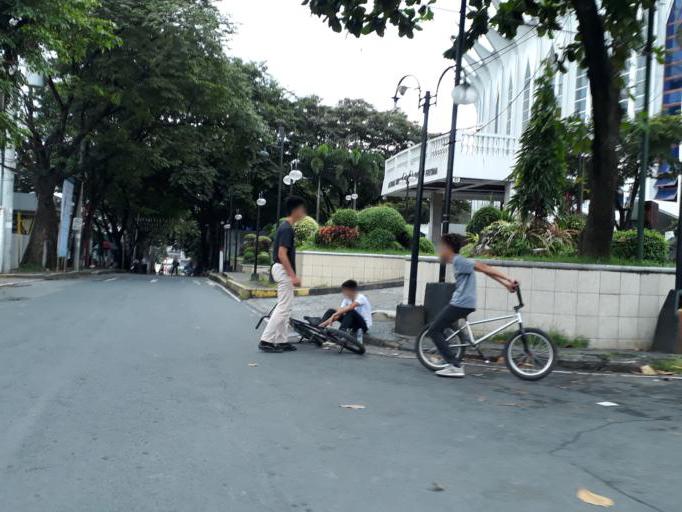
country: PH
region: Calabarzon
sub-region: Province of Rizal
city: Valenzuela
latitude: 14.6826
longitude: 120.9811
